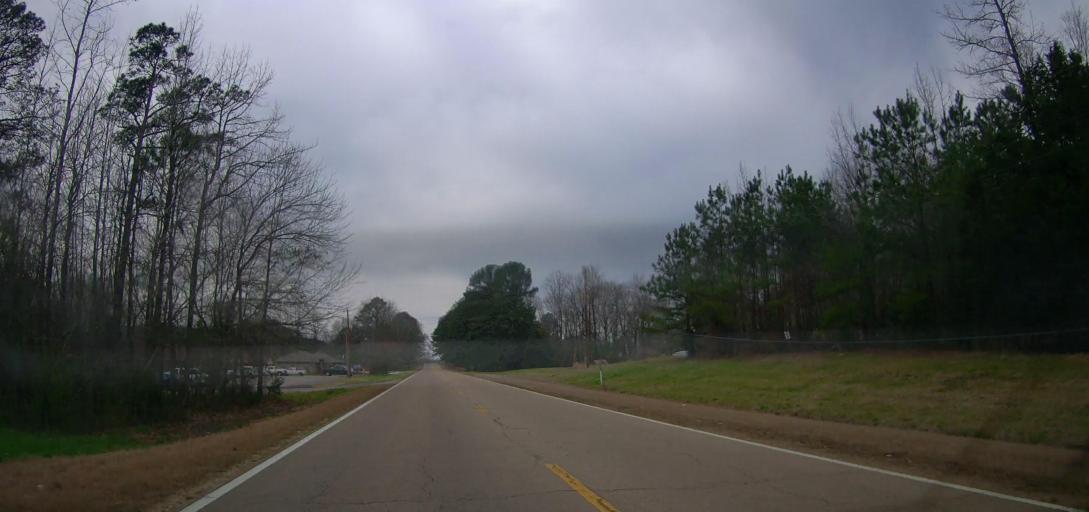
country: US
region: Mississippi
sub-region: Itawamba County
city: Mantachie
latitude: 34.2651
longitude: -88.5464
